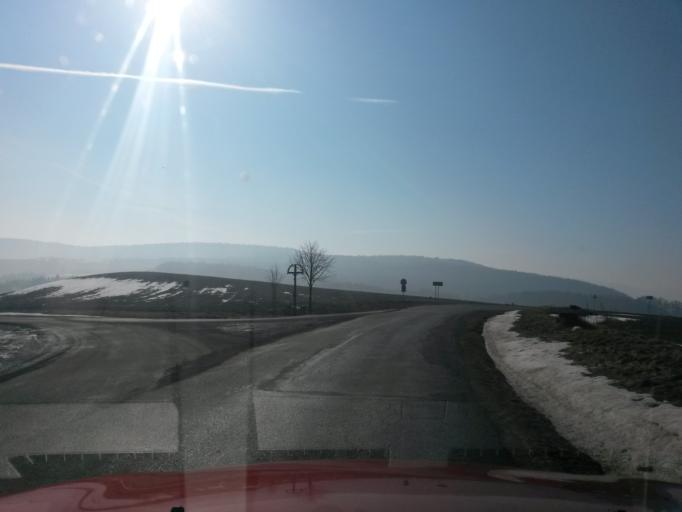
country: SK
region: Kosicky
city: Gelnica
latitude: 48.9287
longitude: 21.0462
